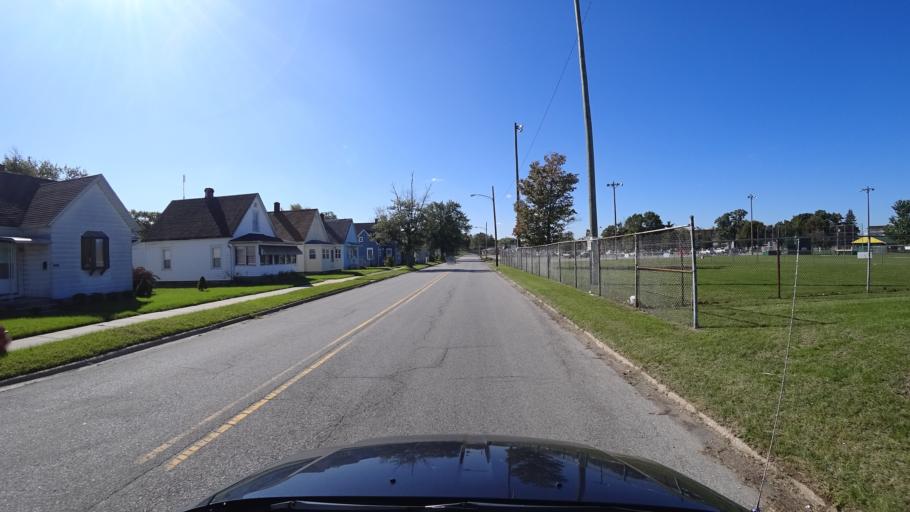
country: US
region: Indiana
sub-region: LaPorte County
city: Michigan City
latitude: 41.7051
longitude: -86.9121
